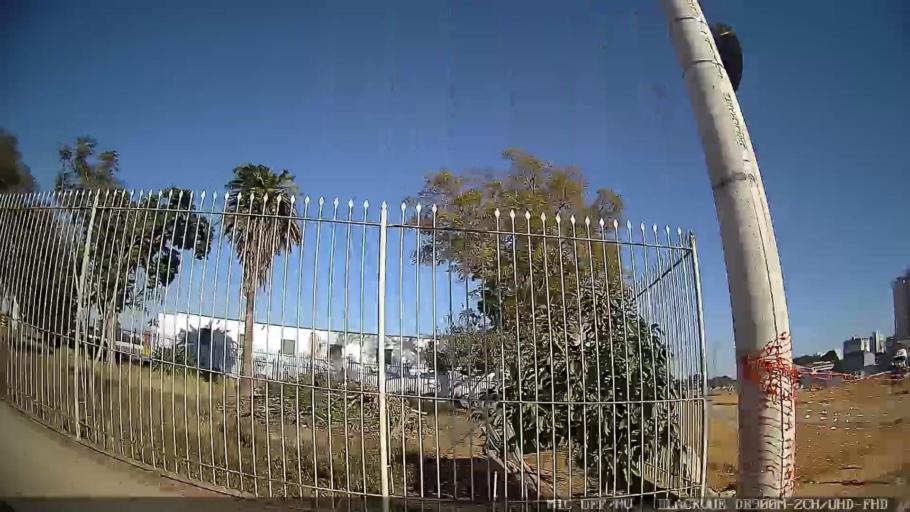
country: BR
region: Sao Paulo
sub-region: Sao Jose Dos Campos
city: Sao Jose dos Campos
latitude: -23.2342
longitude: -45.8979
